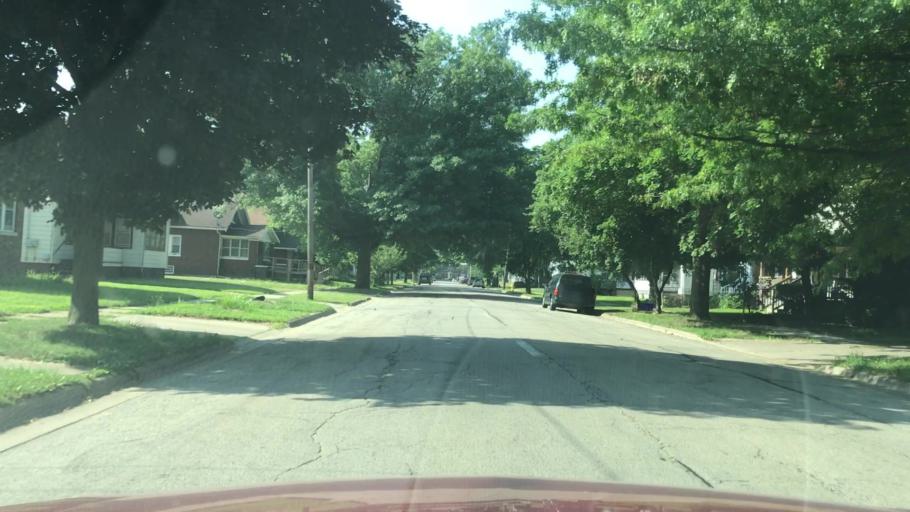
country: US
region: Illinois
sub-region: Winnebago County
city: Rockford
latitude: 42.2451
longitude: -89.0825
